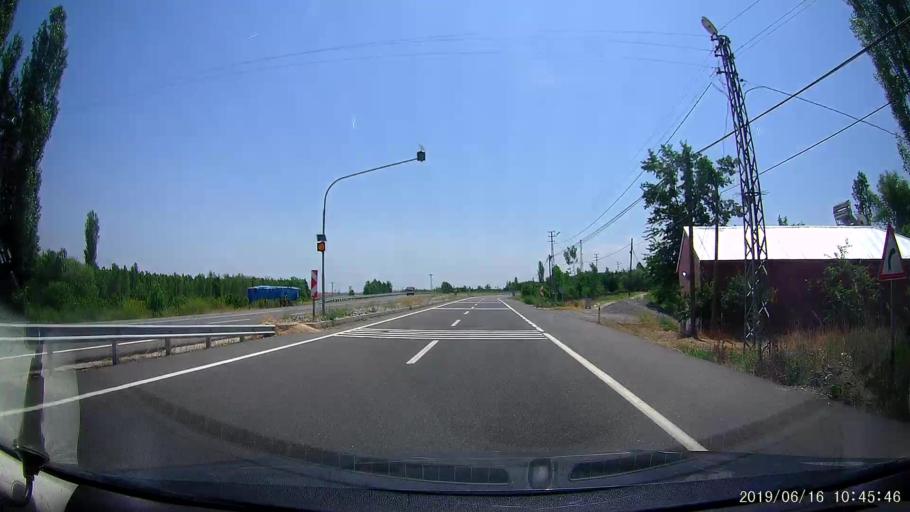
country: AM
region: Armavir
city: Shenavan
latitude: 40.0264
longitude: 43.8732
